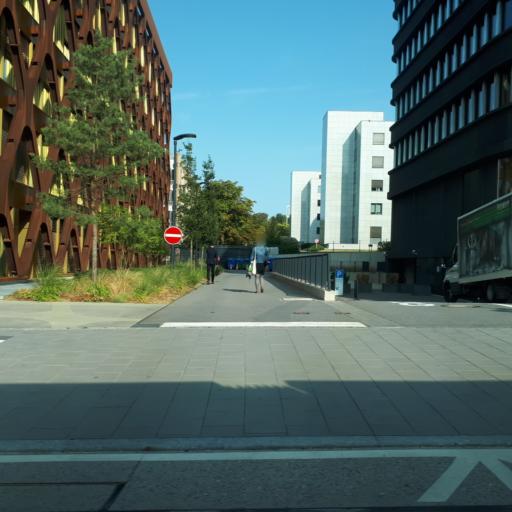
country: LU
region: Luxembourg
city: Kirchberg
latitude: 49.6305
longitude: 6.1679
